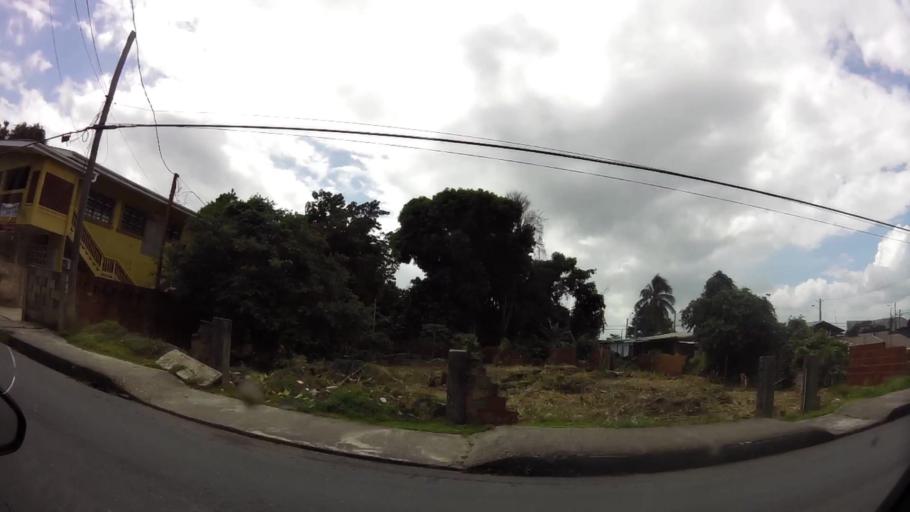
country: TT
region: Tunapuna/Piarco
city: Arouca
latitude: 10.6330
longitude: -61.3261
